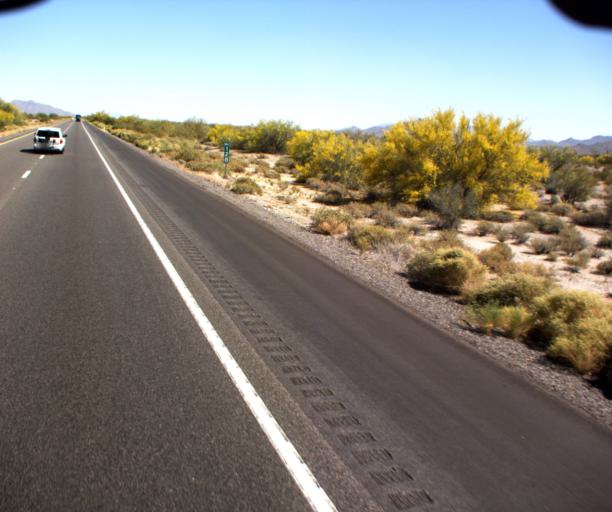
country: US
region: Arizona
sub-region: Maricopa County
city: Gila Bend
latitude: 32.9047
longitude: -112.5277
